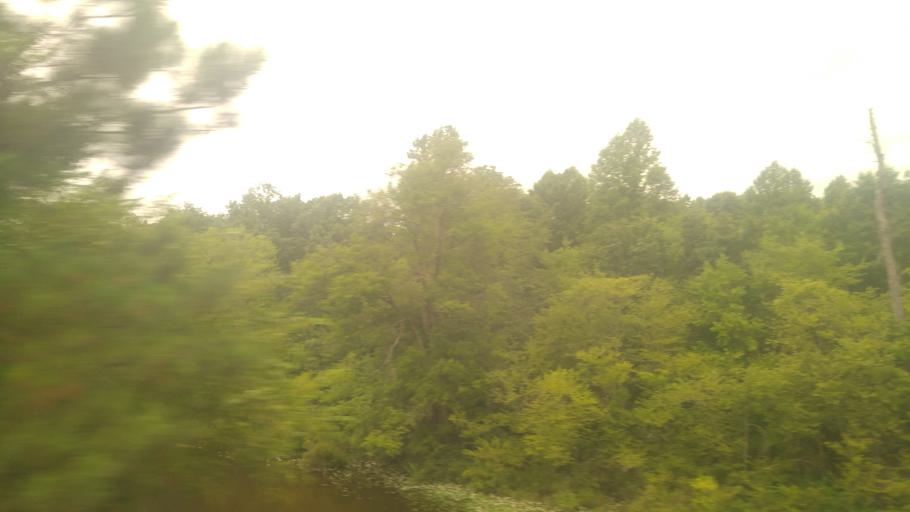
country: US
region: Virginia
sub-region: Henrico County
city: Glen Allen
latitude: 37.7007
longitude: -77.4994
